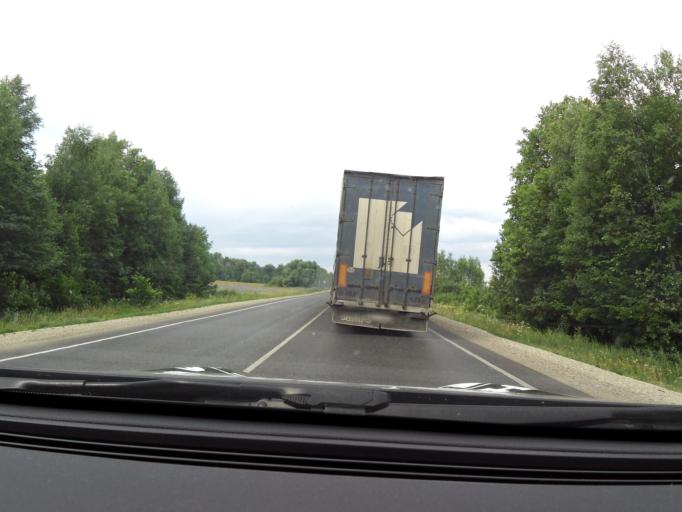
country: RU
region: Bashkortostan
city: Ulu-Telyak
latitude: 54.8513
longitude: 57.1199
